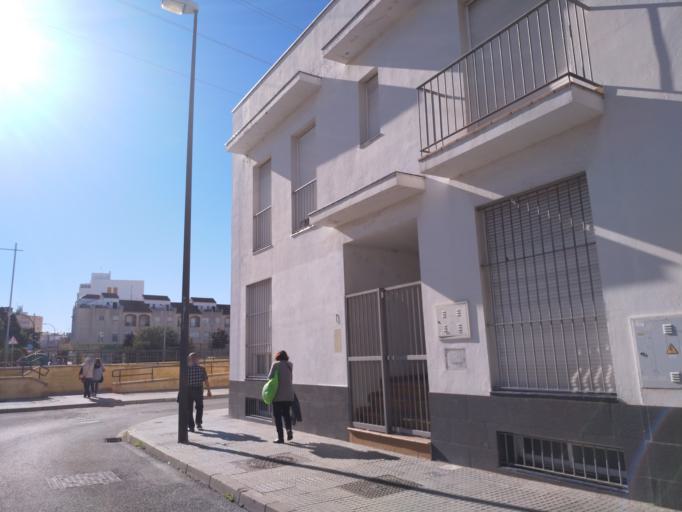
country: ES
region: Andalusia
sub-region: Provincia de Cadiz
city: San Fernando
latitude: 36.4762
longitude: -6.1950
